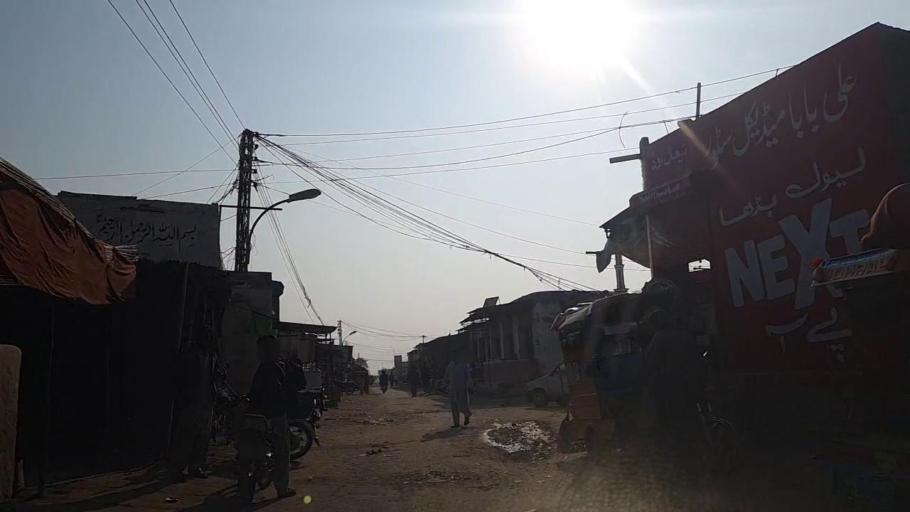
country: PK
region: Sindh
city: Jam Sahib
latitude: 26.2950
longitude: 68.6293
